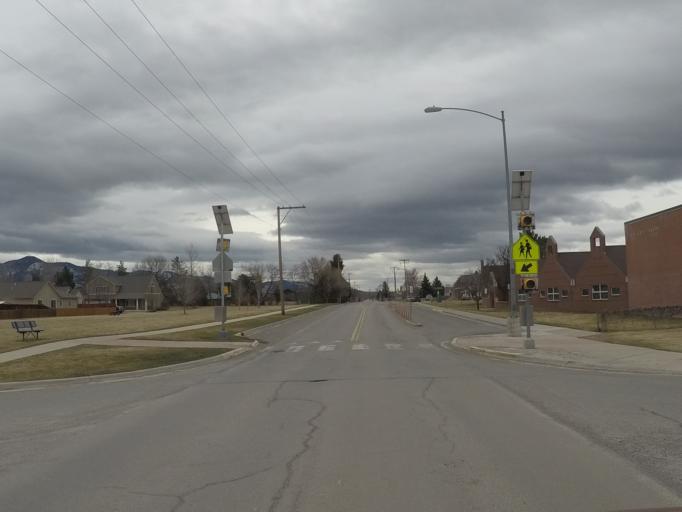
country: US
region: Montana
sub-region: Missoula County
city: Orchard Homes
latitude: 46.8937
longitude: -114.0553
